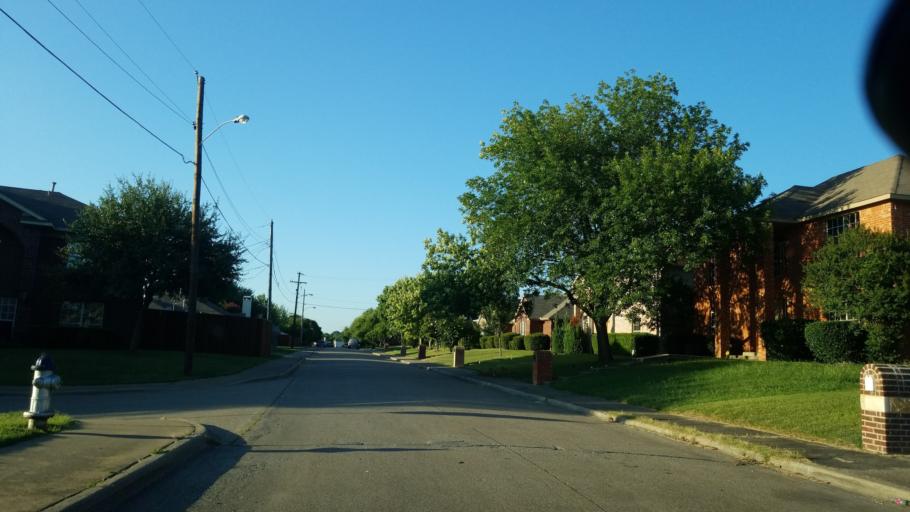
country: US
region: Texas
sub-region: Dallas County
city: Balch Springs
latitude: 32.7801
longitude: -96.6957
